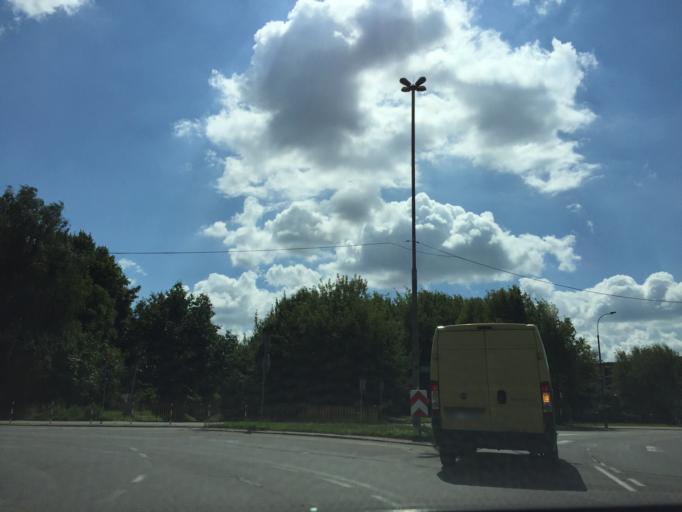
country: PL
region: Podlasie
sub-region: Bialystok
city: Bialystok
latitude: 53.1417
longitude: 23.1579
